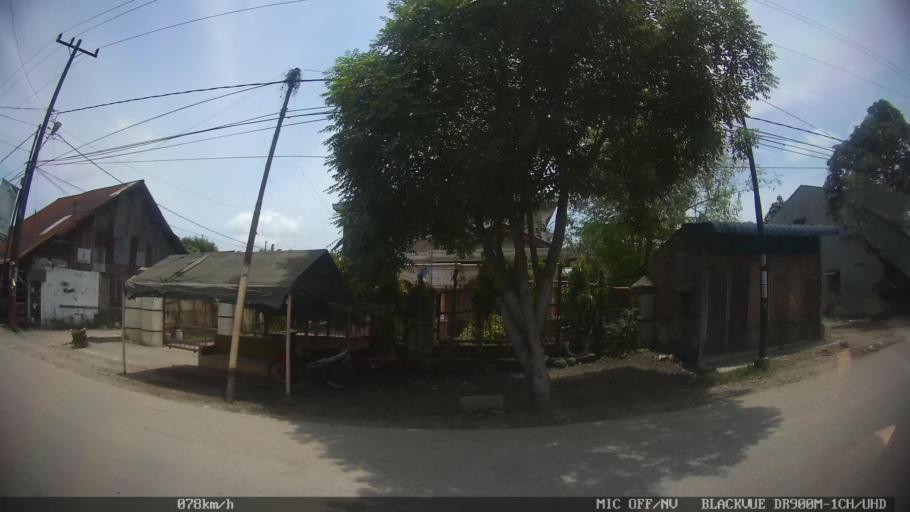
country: ID
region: North Sumatra
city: Labuhan Deli
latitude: 3.7126
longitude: 98.6795
